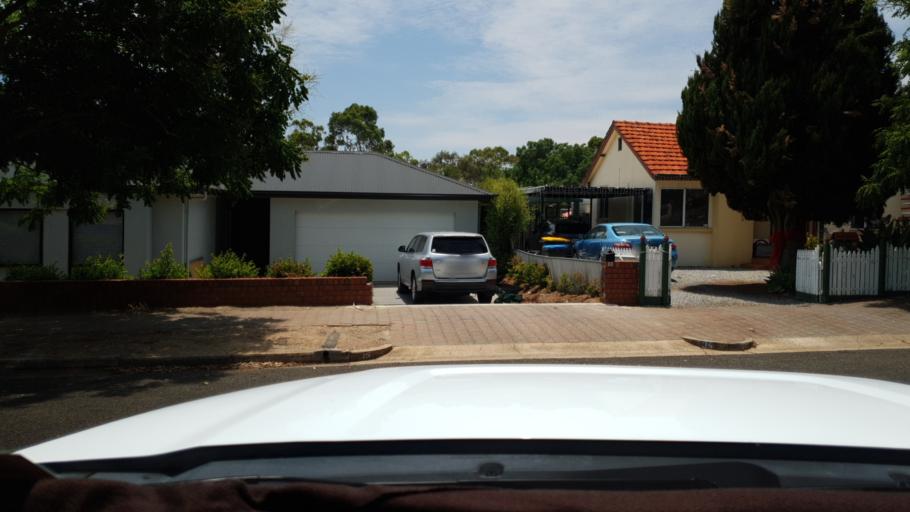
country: AU
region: South Australia
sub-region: Marion
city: Clovelly Park
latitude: -35.0031
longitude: 138.5810
